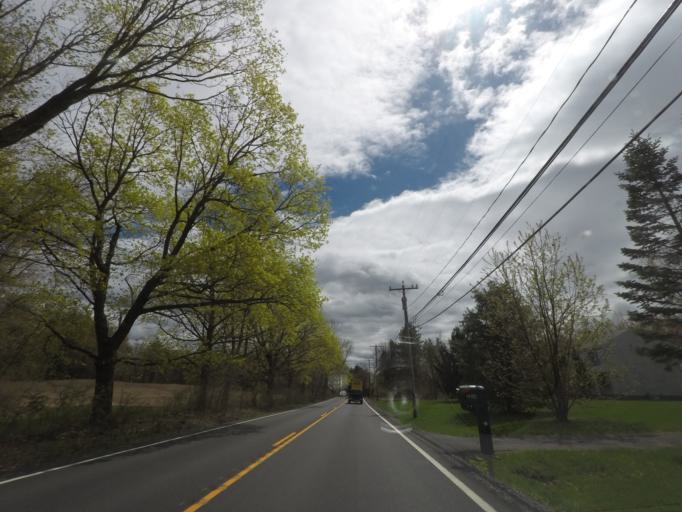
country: US
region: New York
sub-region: Rensselaer County
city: Castleton-on-Hudson
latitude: 42.5206
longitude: -73.7874
